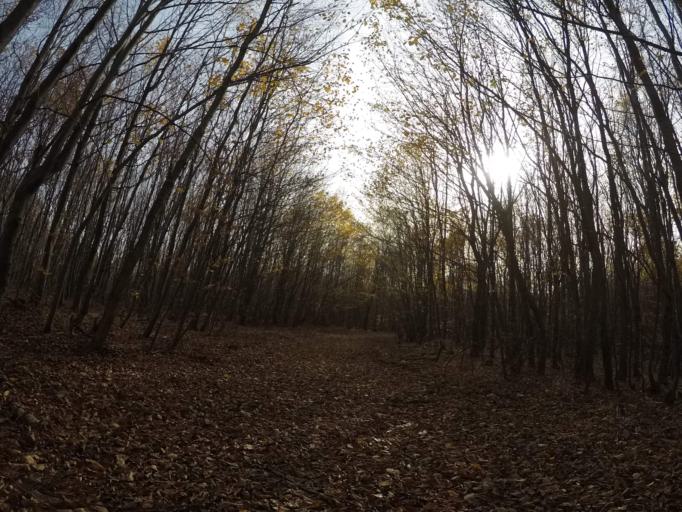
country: SK
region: Presovsky
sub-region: Okres Presov
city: Presov
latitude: 48.9637
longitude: 21.1830
